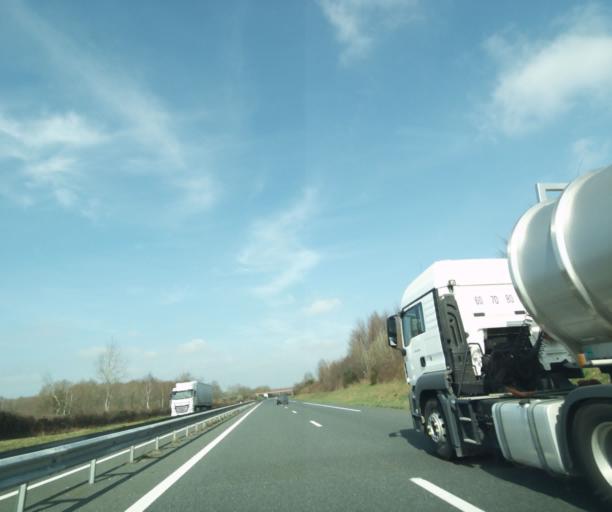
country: FR
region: Centre
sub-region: Departement de l'Indre
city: Chantome
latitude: 46.3925
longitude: 1.4508
